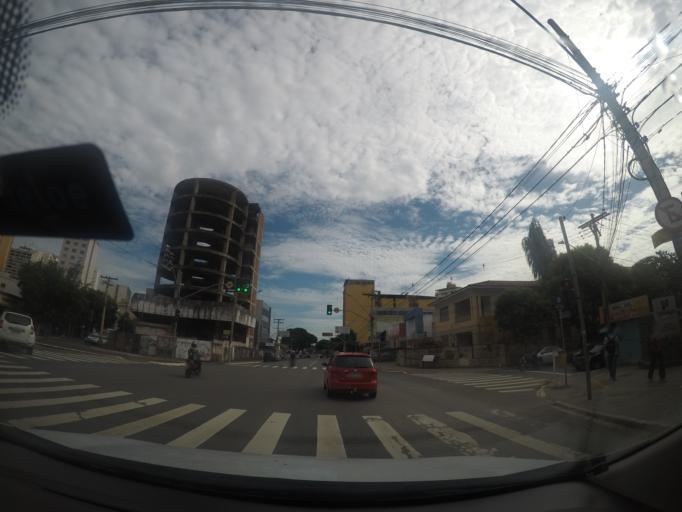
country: BR
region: Goias
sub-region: Goiania
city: Goiania
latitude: -16.6770
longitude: -49.2555
